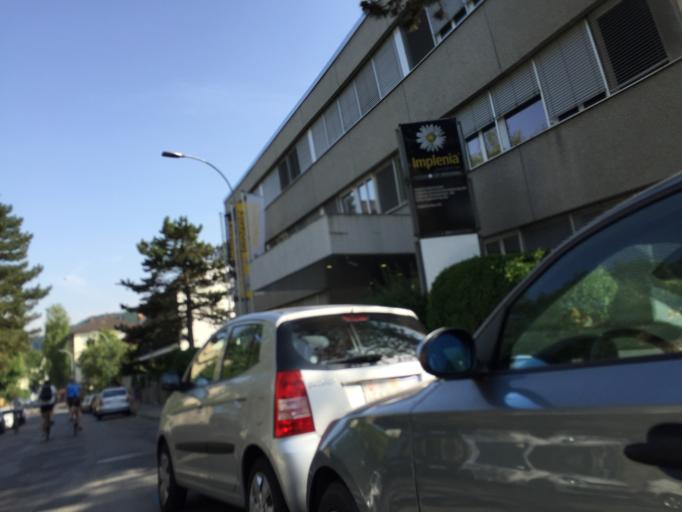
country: CH
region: Bern
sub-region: Bern-Mittelland District
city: Bern
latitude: 46.9387
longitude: 7.4378
